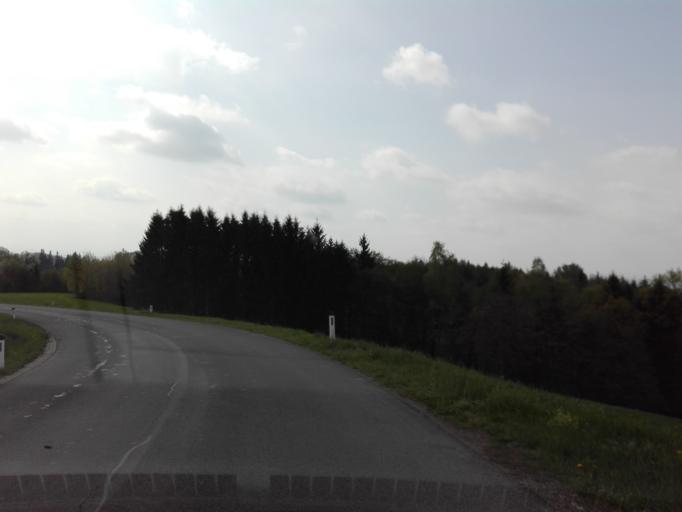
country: AT
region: Upper Austria
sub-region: Politischer Bezirk Perg
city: Perg
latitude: 48.2569
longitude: 14.6997
